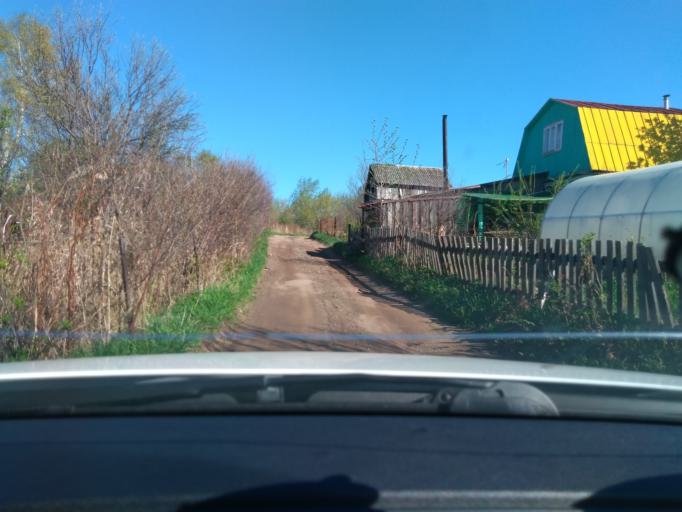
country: RU
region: Perm
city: Lobanovo
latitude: 57.8683
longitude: 56.3039
